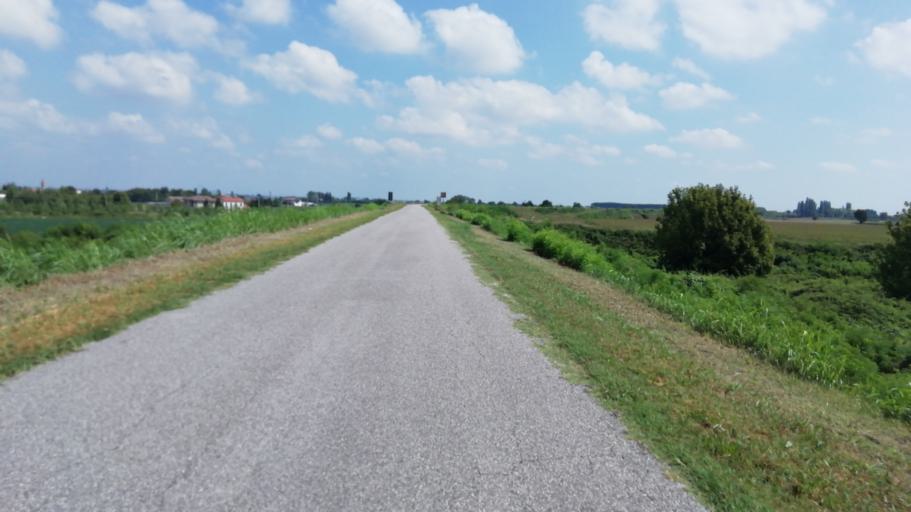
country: IT
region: Veneto
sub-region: Provincia di Rovigo
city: Gaiba
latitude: 44.9430
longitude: 11.4973
